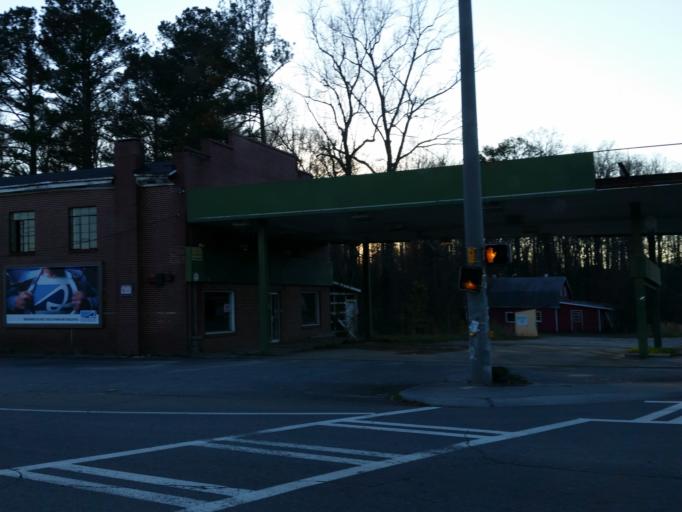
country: US
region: Georgia
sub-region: Cherokee County
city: Holly Springs
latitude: 34.1766
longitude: -84.4203
